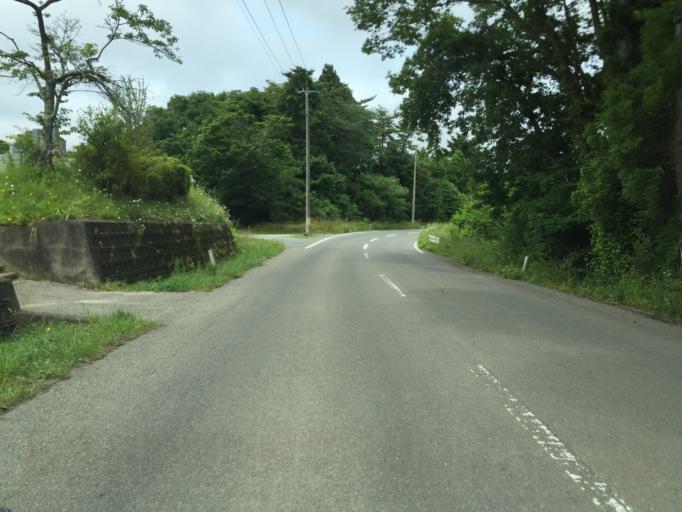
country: JP
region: Fukushima
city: Namie
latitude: 37.7215
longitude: 140.9802
